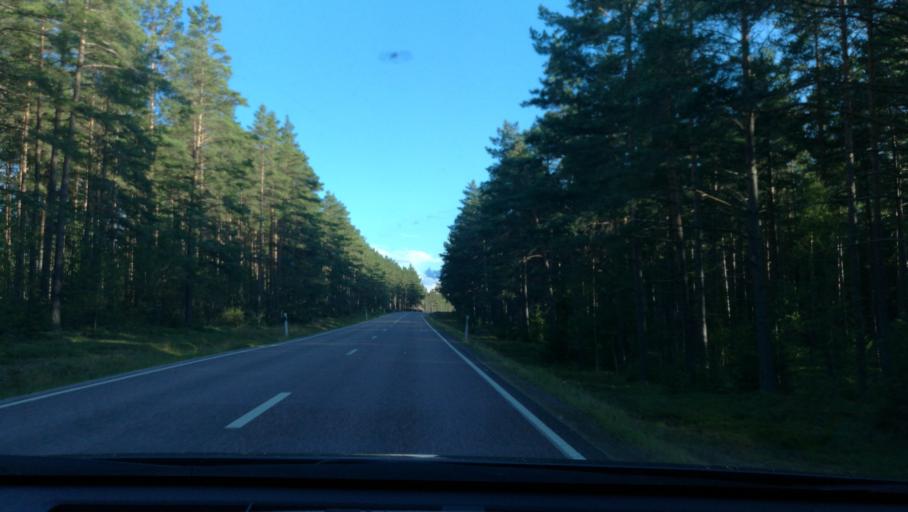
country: SE
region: Vaestmanland
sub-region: Kungsors Kommun
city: Kungsoer
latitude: 59.3196
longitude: 16.1097
